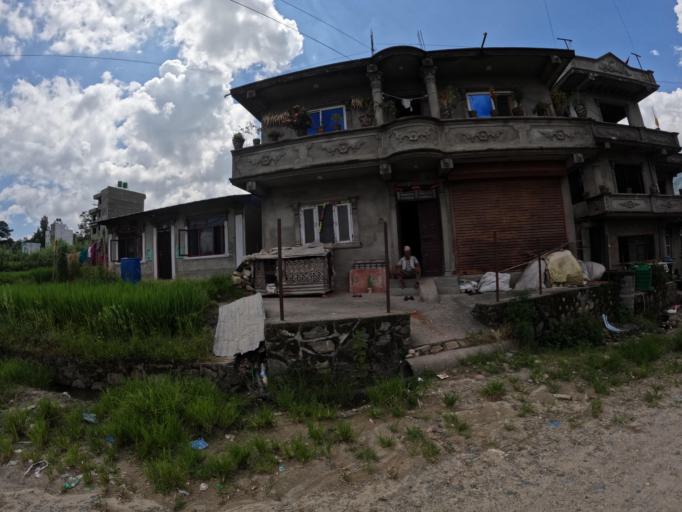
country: NP
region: Central Region
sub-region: Bagmati Zone
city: Kathmandu
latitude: 27.7777
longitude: 85.3288
